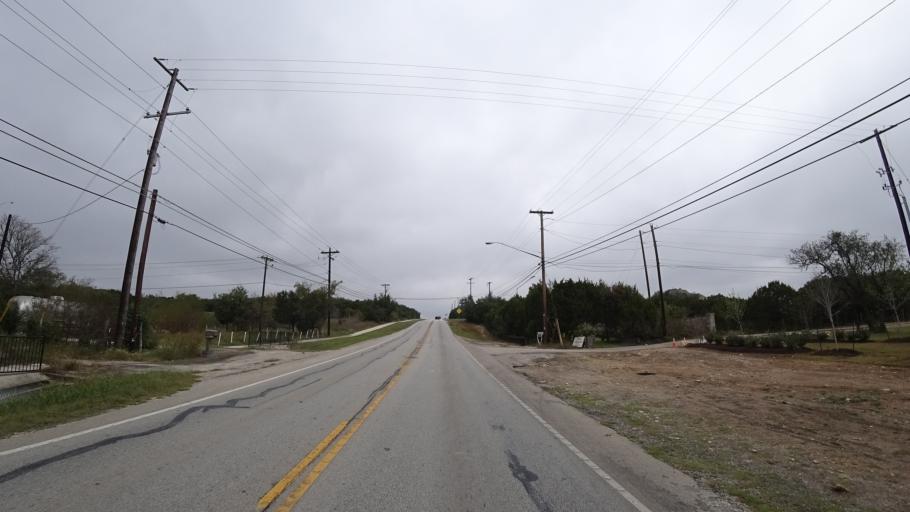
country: US
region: Texas
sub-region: Travis County
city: Shady Hollow
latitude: 30.2228
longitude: -97.8921
